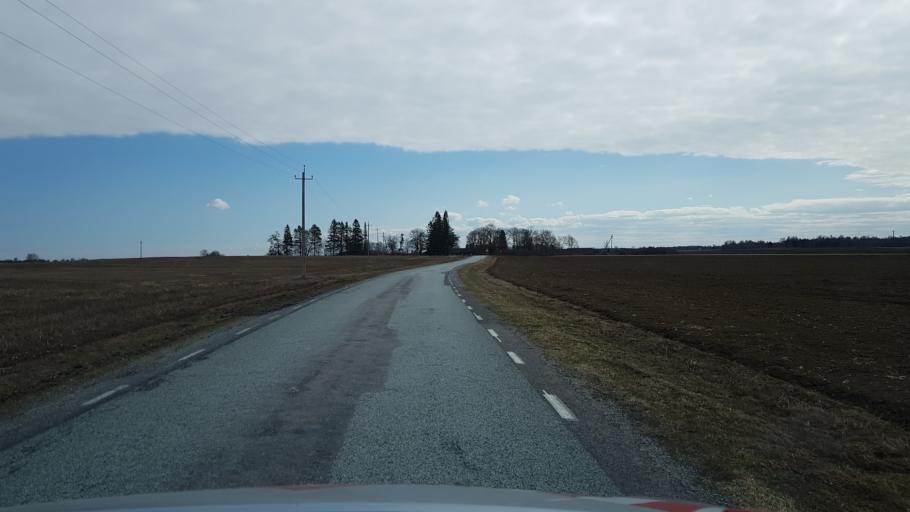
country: EE
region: Laeaene-Virumaa
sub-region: Haljala vald
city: Haljala
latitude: 59.4259
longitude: 26.2216
